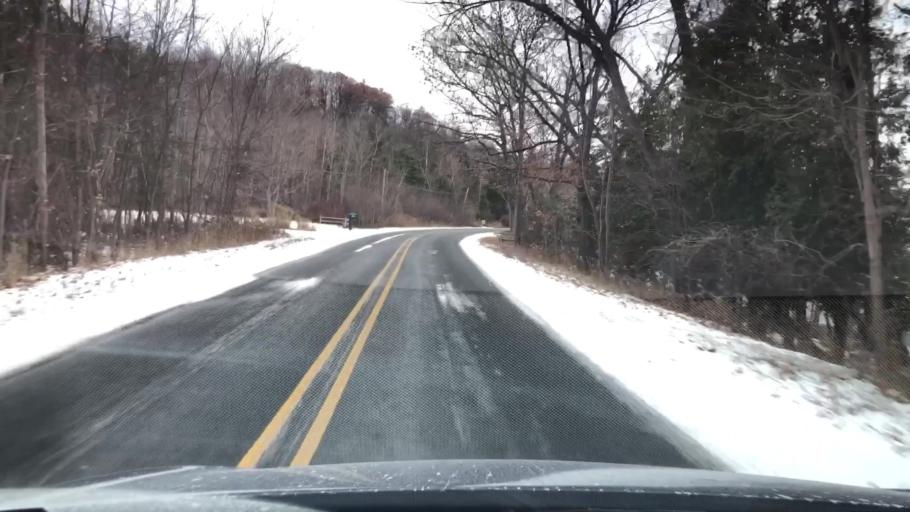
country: US
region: Michigan
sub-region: Grand Traverse County
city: Traverse City
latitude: 44.8324
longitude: -85.5635
